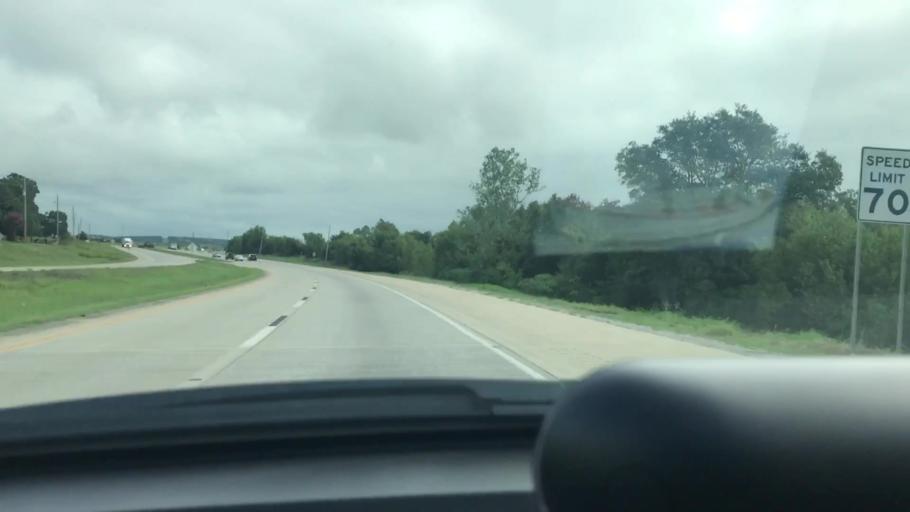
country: US
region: Oklahoma
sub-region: Atoka County
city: Atoka
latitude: 34.4006
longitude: -96.1167
